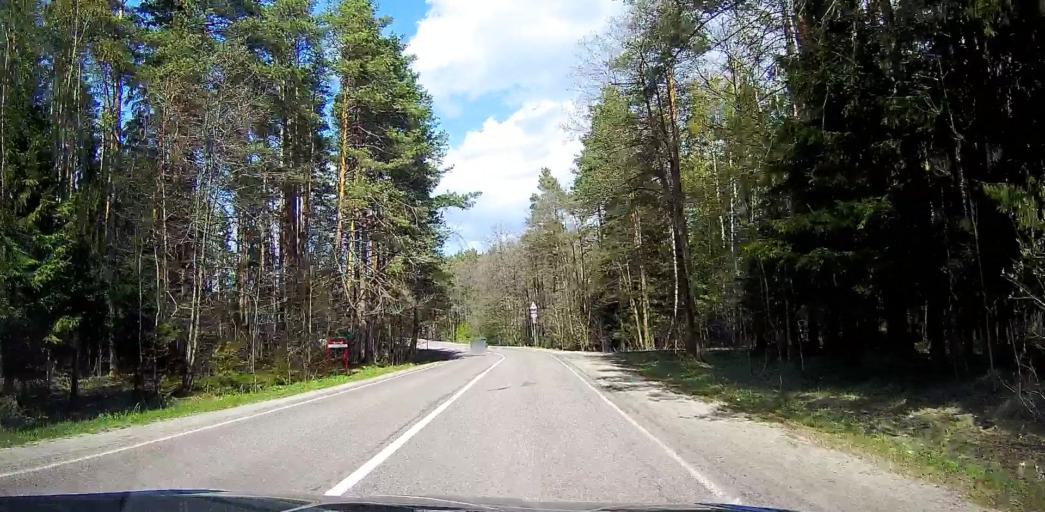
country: RU
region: Moskovskaya
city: Davydovo
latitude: 55.5688
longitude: 38.8226
